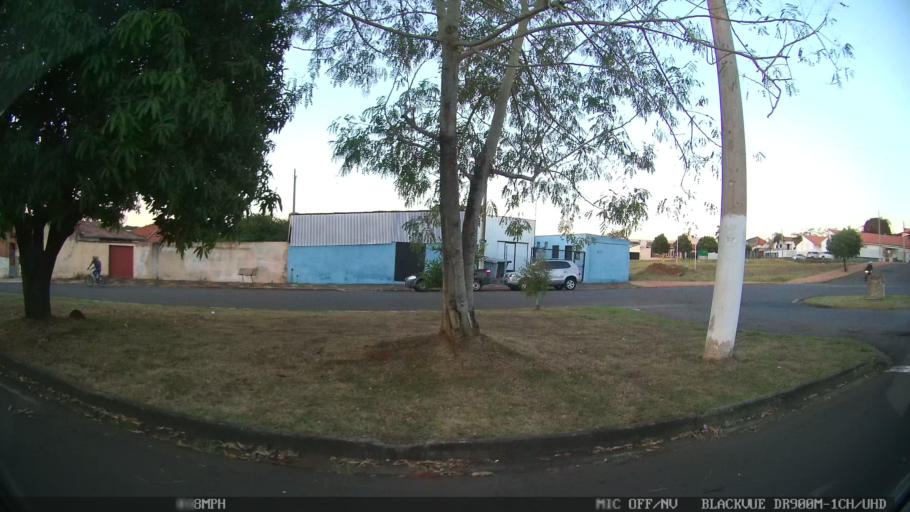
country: BR
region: Sao Paulo
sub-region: Santa Barbara D'Oeste
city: Santa Barbara d'Oeste
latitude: -22.7587
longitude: -47.4047
